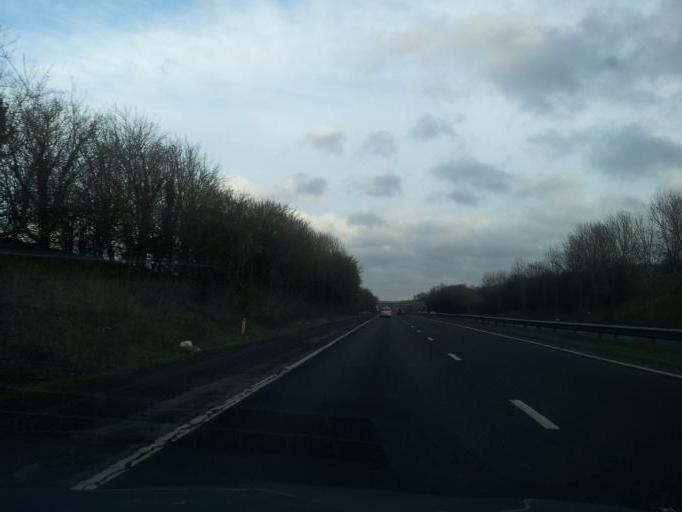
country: GB
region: England
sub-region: Hertfordshire
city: Tring
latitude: 51.7880
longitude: -0.6637
